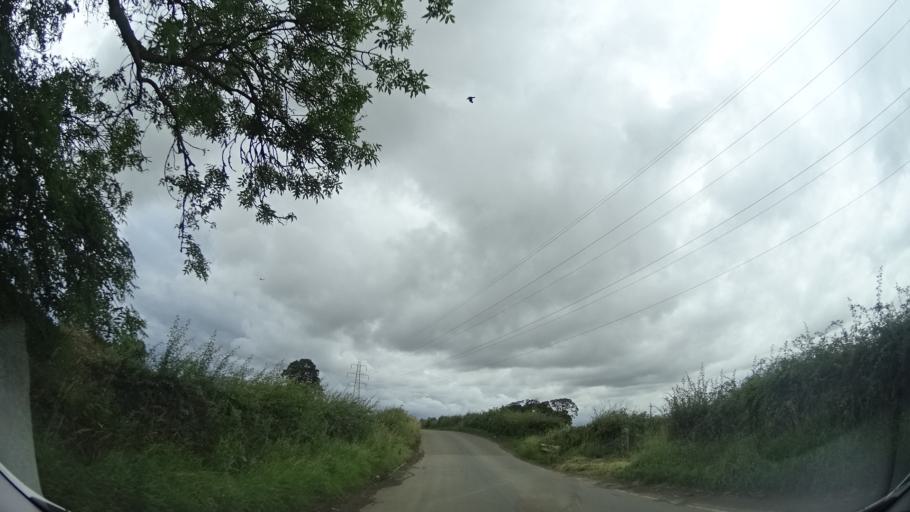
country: GB
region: Scotland
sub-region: West Lothian
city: Kirknewton
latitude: 55.9053
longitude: -3.4356
